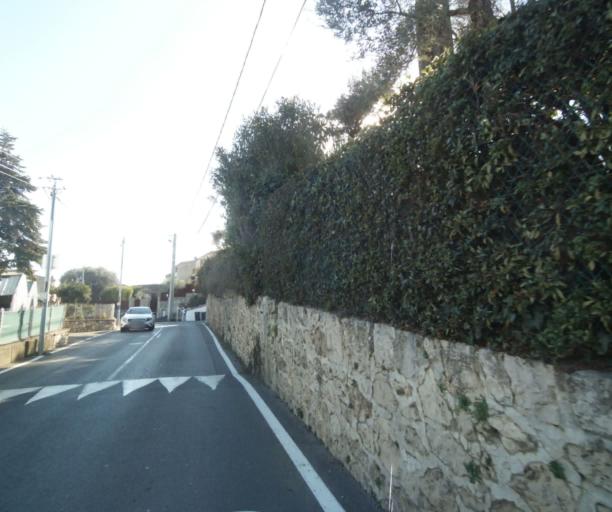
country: FR
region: Provence-Alpes-Cote d'Azur
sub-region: Departement des Alpes-Maritimes
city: Biot
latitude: 43.6028
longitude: 7.1079
